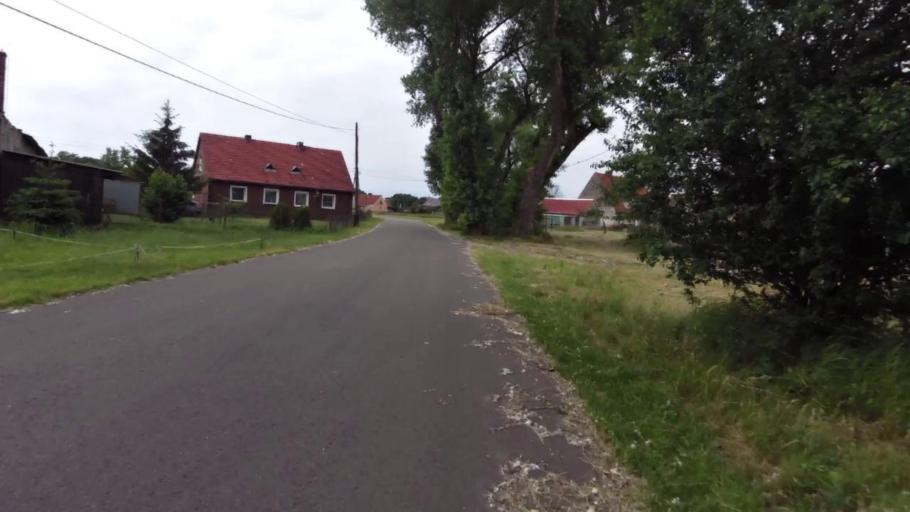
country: PL
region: West Pomeranian Voivodeship
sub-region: Powiat goleniowski
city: Stepnica
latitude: 53.7191
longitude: 14.5613
